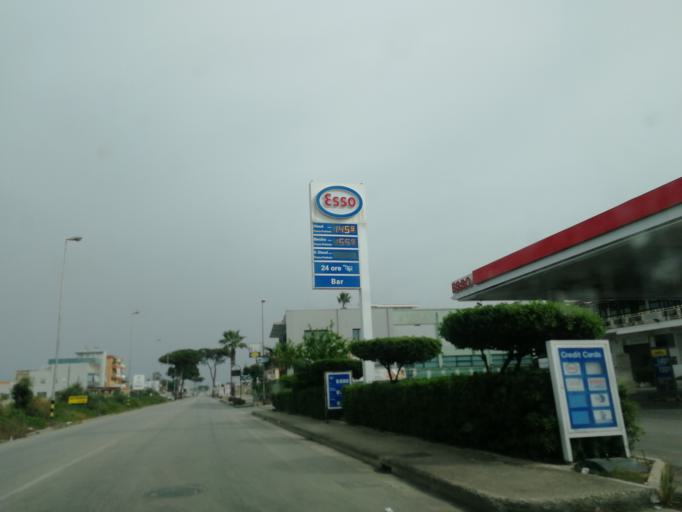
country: IT
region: Apulia
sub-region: Provincia di Barletta - Andria - Trani
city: Barletta
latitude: 41.3124
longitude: 16.3056
